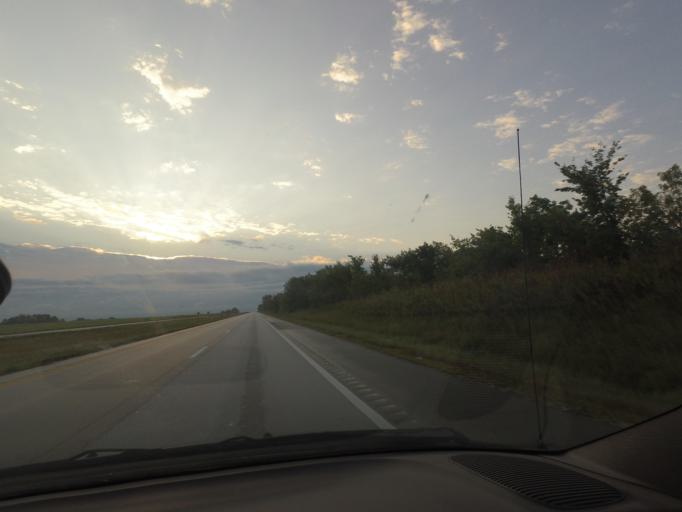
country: US
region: Missouri
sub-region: Shelby County
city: Shelbina
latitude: 39.7303
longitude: -92.1971
